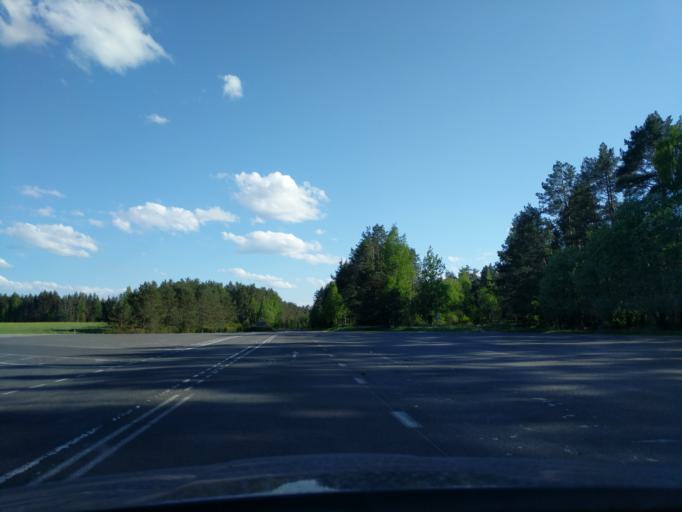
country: BY
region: Minsk
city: Myadzyel
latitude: 54.8282
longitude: 26.9417
